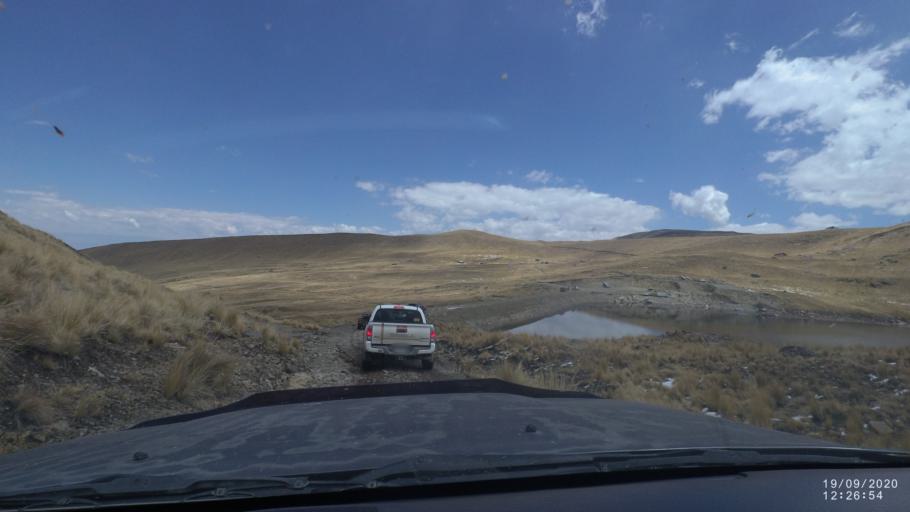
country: BO
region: Cochabamba
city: Cochabamba
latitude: -17.2945
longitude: -66.1121
